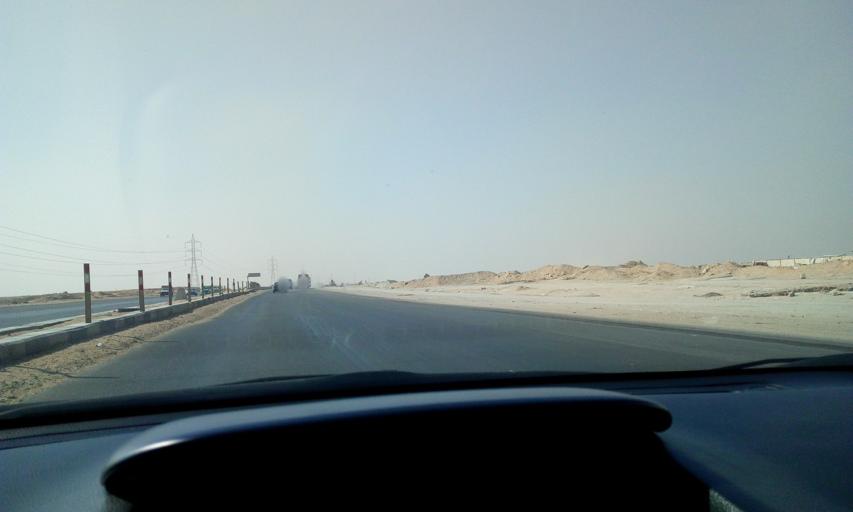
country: EG
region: Al Jizah
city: Madinat Sittah Uktubar
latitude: 29.8718
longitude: 31.0741
